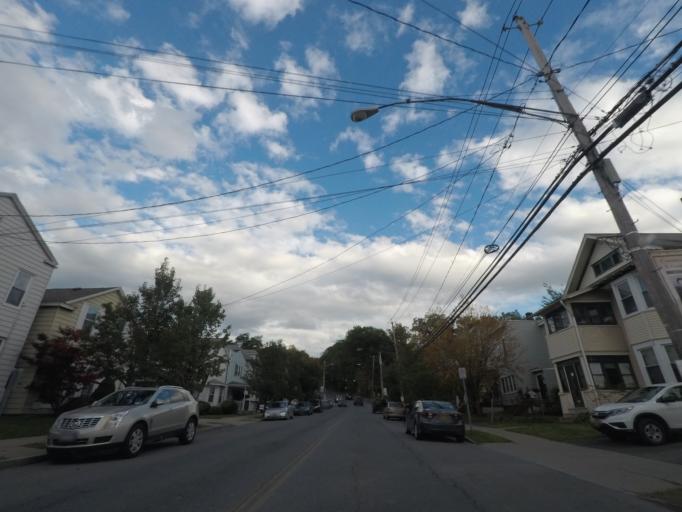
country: US
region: New York
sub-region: Rensselaer County
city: Rensselaer
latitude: 42.6366
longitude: -73.7380
